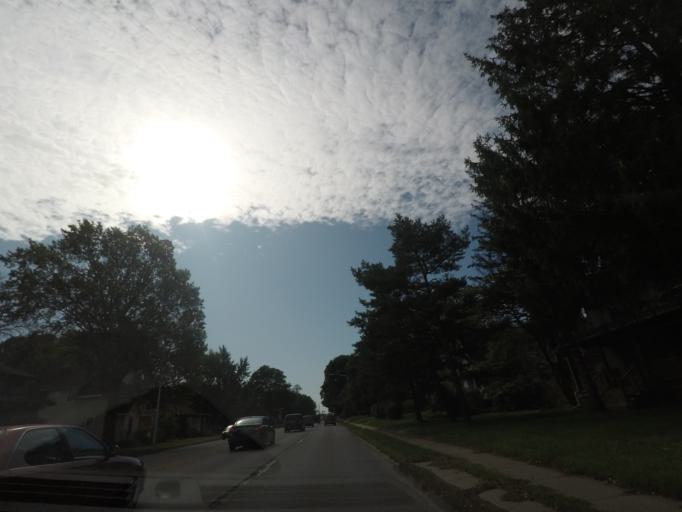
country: US
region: Iowa
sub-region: Story County
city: Ames
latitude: 42.0300
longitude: -93.6204
